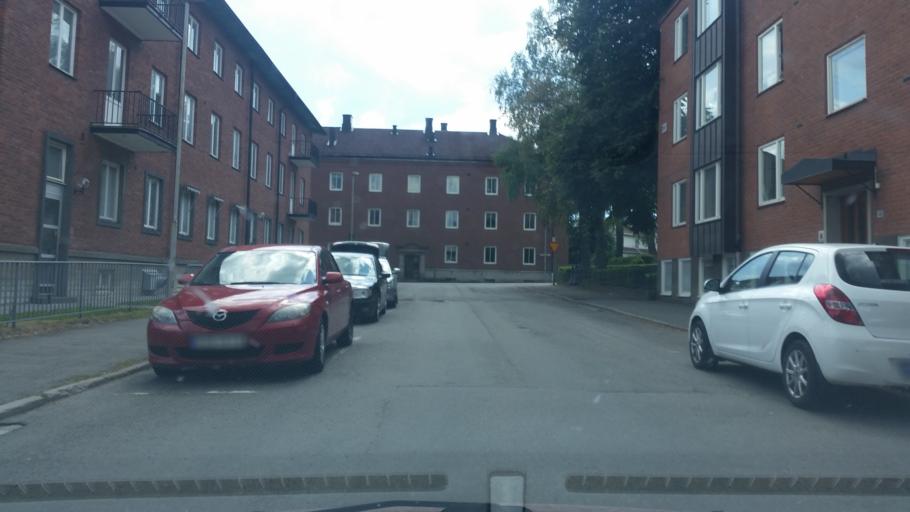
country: SE
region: Vaestra Goetaland
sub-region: Skovde Kommun
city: Skoevde
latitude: 58.3877
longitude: 13.8435
